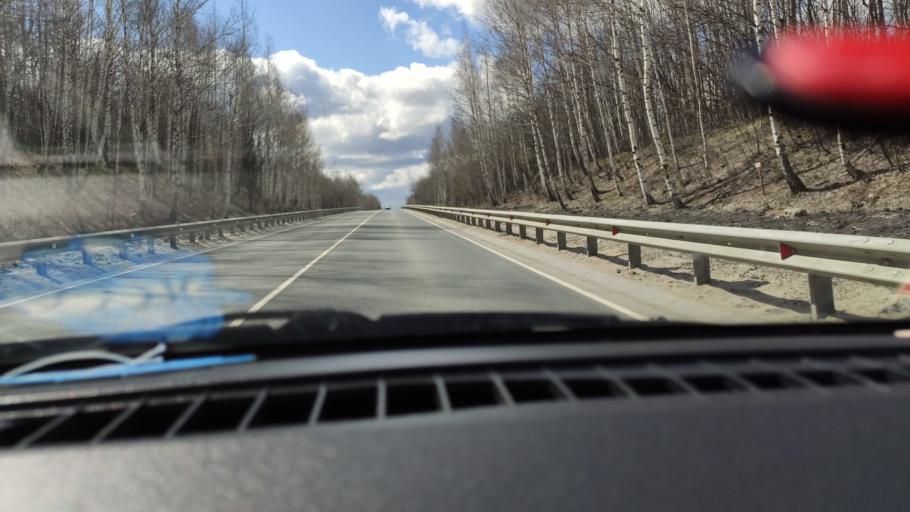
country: RU
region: Saratov
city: Khvalynsk
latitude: 52.4519
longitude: 48.0124
